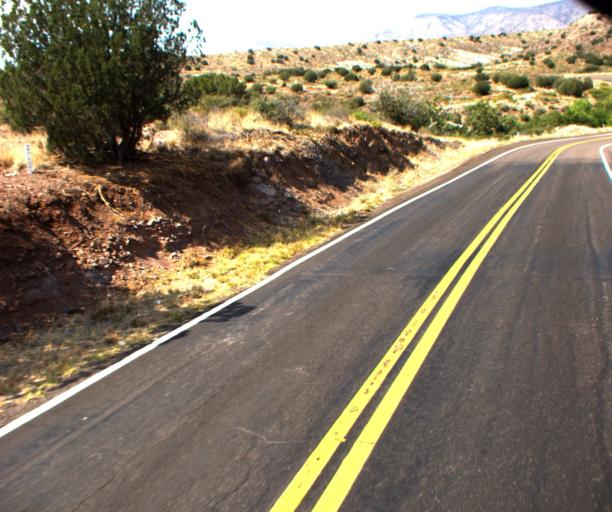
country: US
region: Arizona
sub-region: Greenlee County
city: Clifton
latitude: 33.0239
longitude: -109.1411
